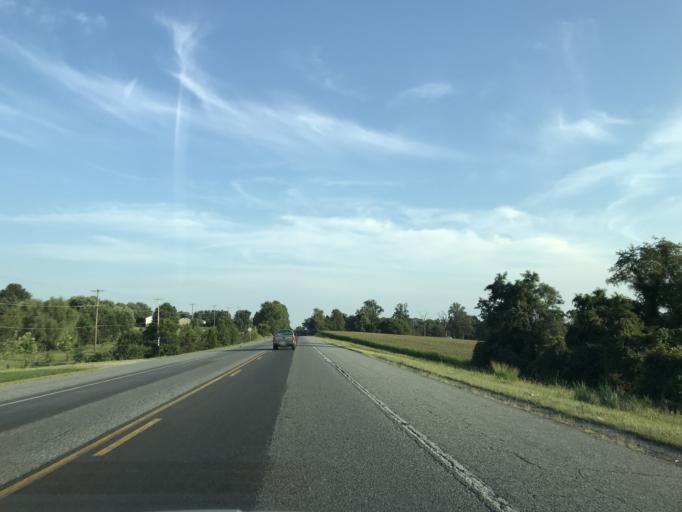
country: US
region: Maryland
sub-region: Cecil County
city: North East
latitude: 39.6620
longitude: -75.9552
